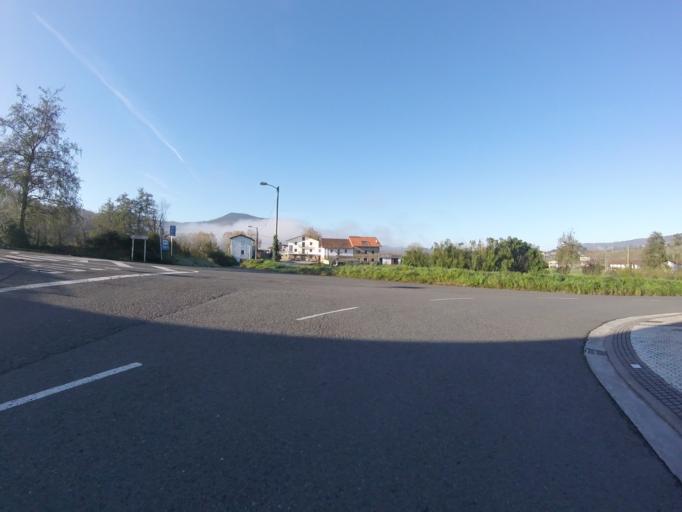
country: ES
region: Basque Country
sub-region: Provincia de Guipuzcoa
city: Lasarte
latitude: 43.2702
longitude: -2.0335
